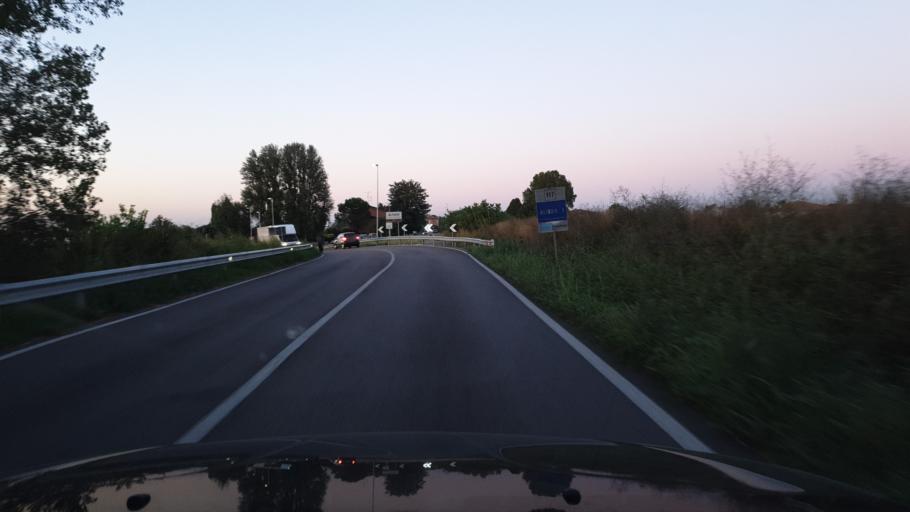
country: IT
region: Emilia-Romagna
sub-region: Provincia di Bologna
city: Altedo
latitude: 44.6594
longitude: 11.4911
